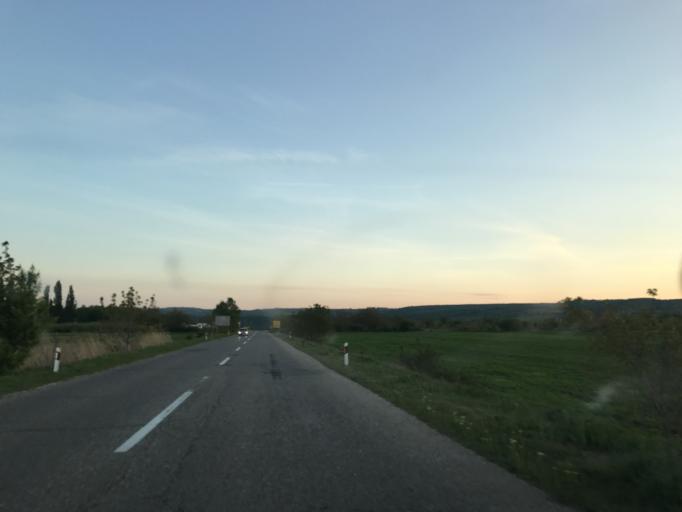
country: RS
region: Central Serbia
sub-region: Borski Okrug
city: Negotin
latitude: 44.2442
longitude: 22.5172
